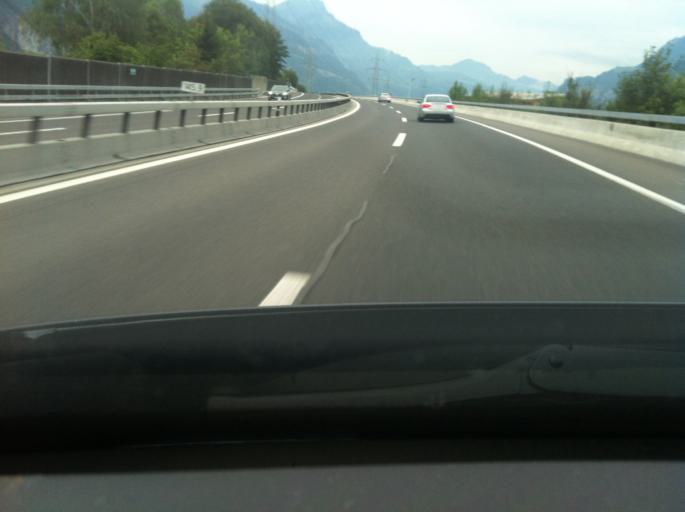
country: CH
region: Uri
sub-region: Uri
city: Attinghausen
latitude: 46.8642
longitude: 8.6335
